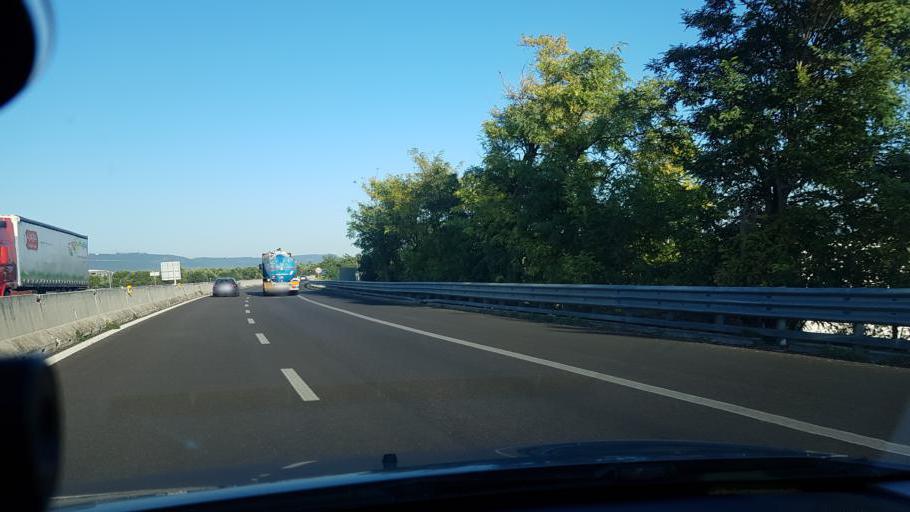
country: IT
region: Apulia
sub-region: Provincia di Brindisi
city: Fasano
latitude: 40.8418
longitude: 17.3681
